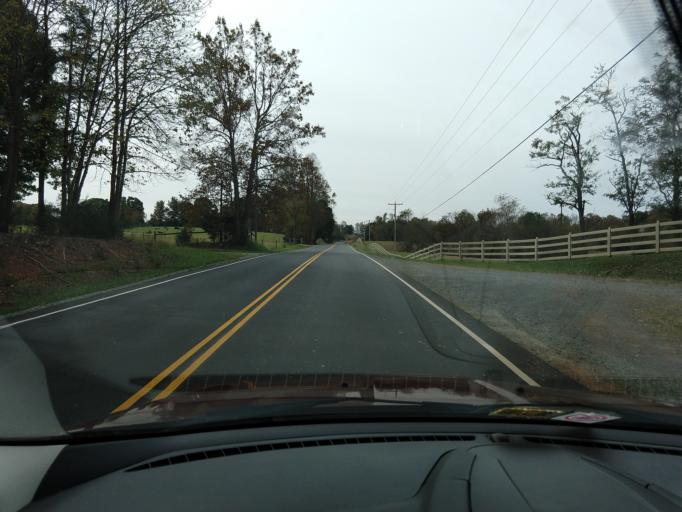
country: US
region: Virginia
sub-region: Franklin County
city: Union Hall
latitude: 36.9858
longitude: -79.7295
